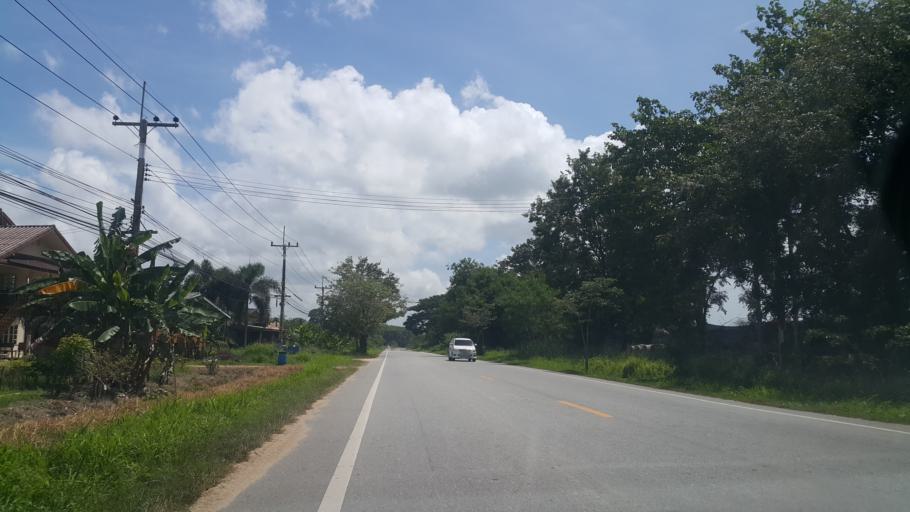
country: TH
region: Rayong
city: Ban Chang
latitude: 12.7954
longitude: 101.0441
